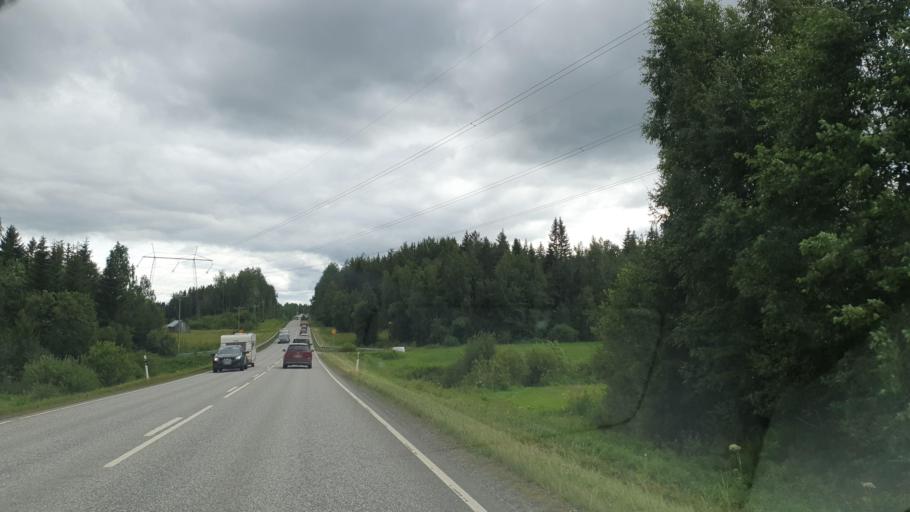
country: FI
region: Northern Savo
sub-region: Ylae-Savo
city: Sonkajaervi
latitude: 63.7078
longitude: 27.3583
